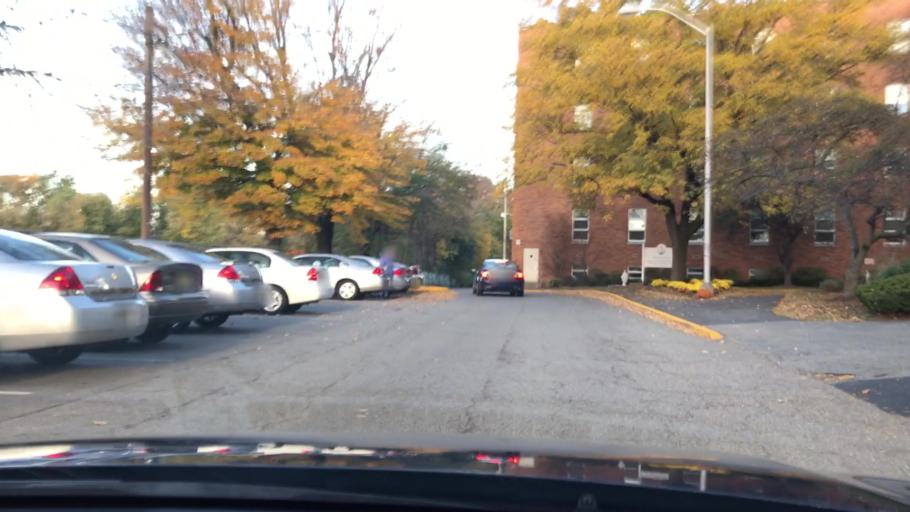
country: US
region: New Jersey
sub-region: Bergen County
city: Hasbrouck Heights
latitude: 40.8660
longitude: -74.0953
